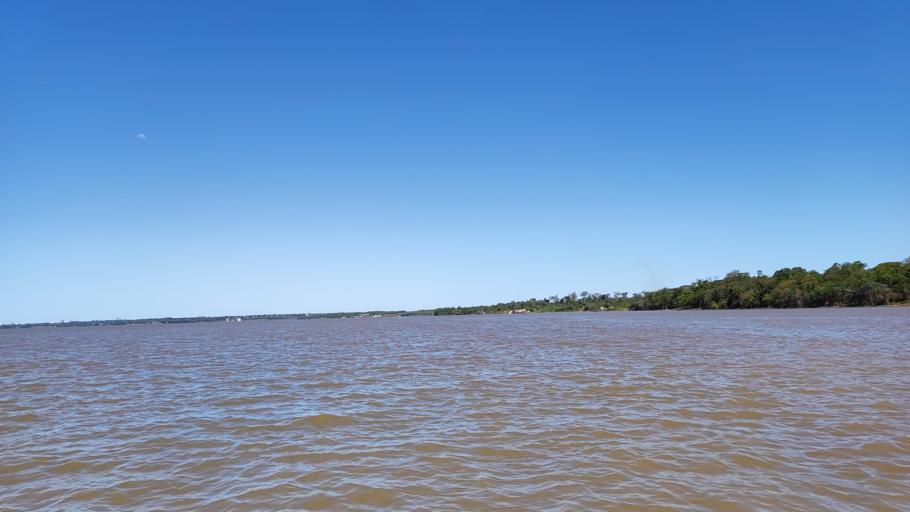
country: PY
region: Itapua
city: San Juan del Parana
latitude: -27.3513
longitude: -56.0052
